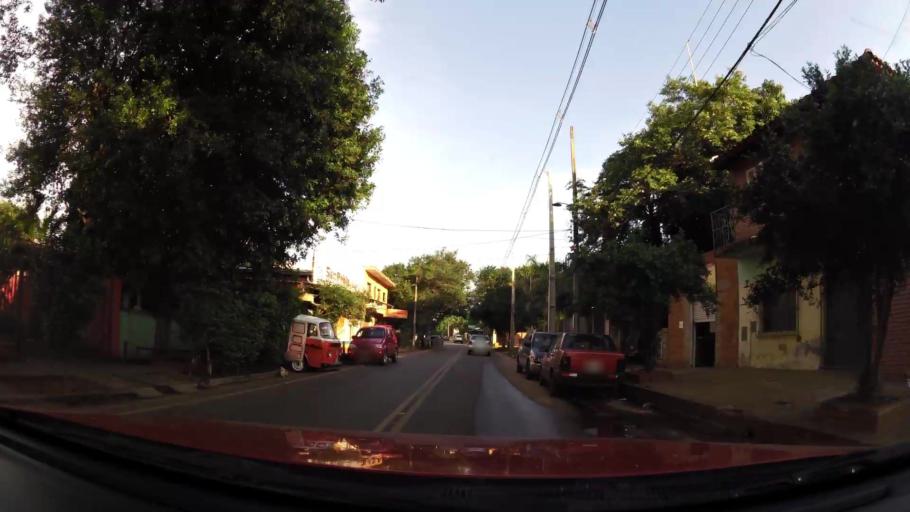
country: PY
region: Central
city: San Lorenzo
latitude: -25.3585
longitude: -57.5133
